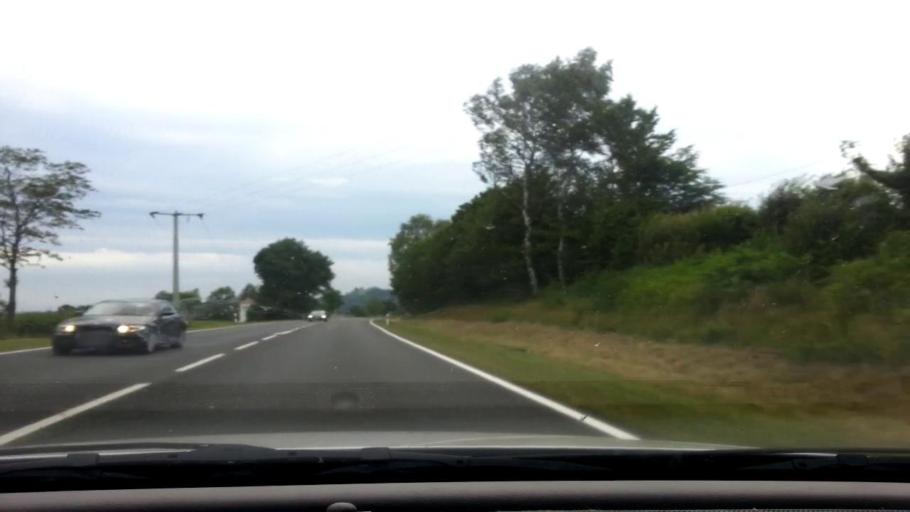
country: DE
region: Bavaria
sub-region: Upper Palatinate
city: Erbendorf
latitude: 49.8533
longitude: 11.9745
